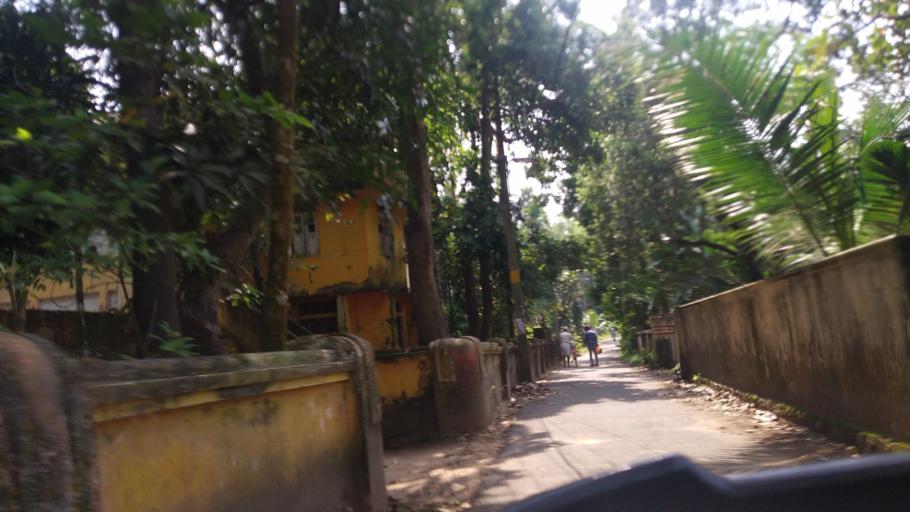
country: IN
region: Kerala
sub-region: Ernakulam
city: Elur
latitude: 10.0562
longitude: 76.2179
